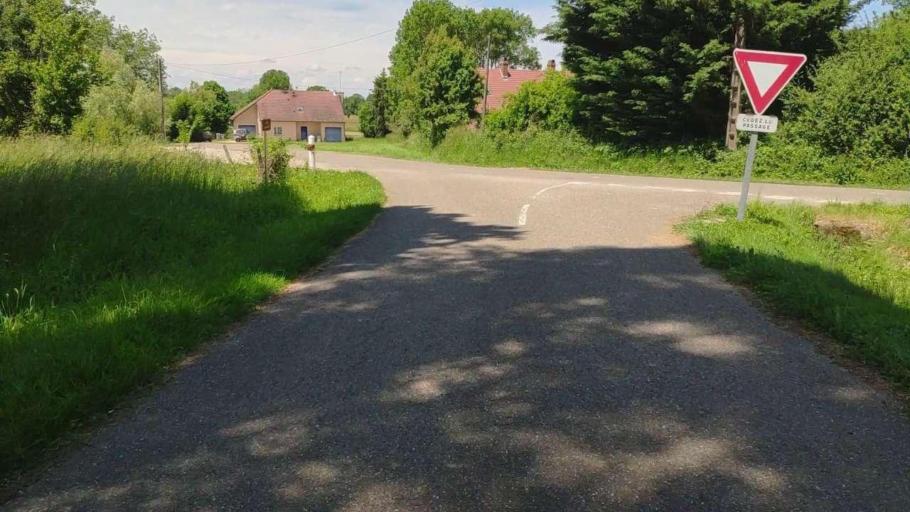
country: FR
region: Franche-Comte
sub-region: Departement du Jura
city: Bletterans
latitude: 46.8046
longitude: 5.3819
